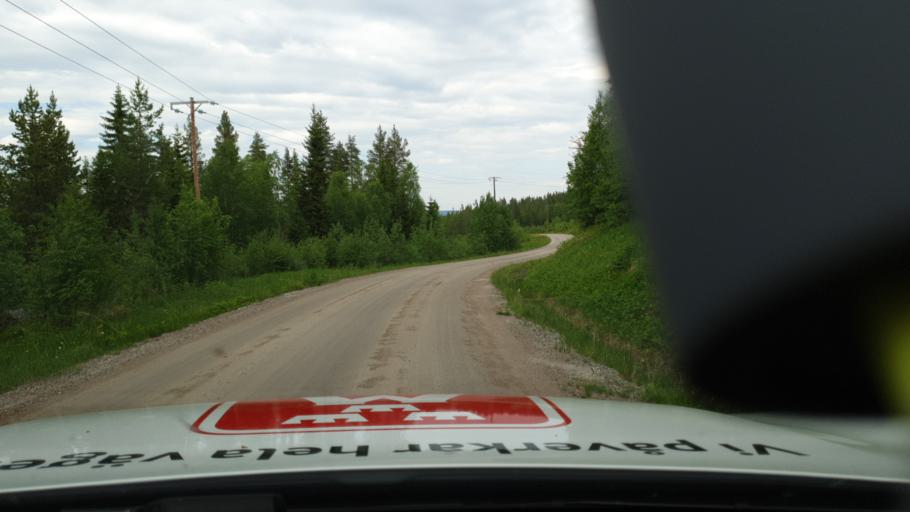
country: SE
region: Jaemtland
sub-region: Braecke Kommun
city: Braecke
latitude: 63.0874
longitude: 15.7332
